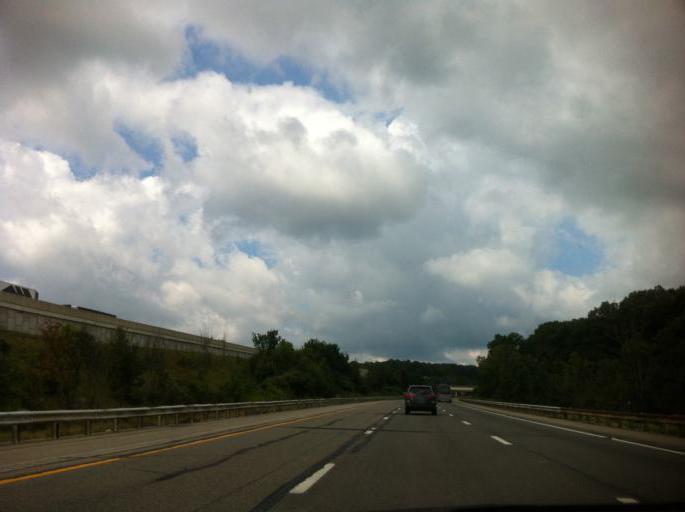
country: US
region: Ohio
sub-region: Summit County
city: Peninsula
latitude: 41.2524
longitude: -81.5790
